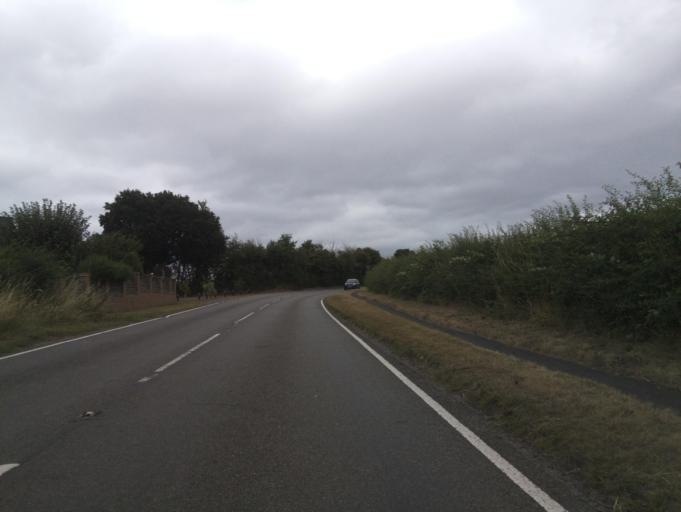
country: GB
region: England
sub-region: Leicestershire
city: Donisthorpe
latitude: 52.7148
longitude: -1.5532
